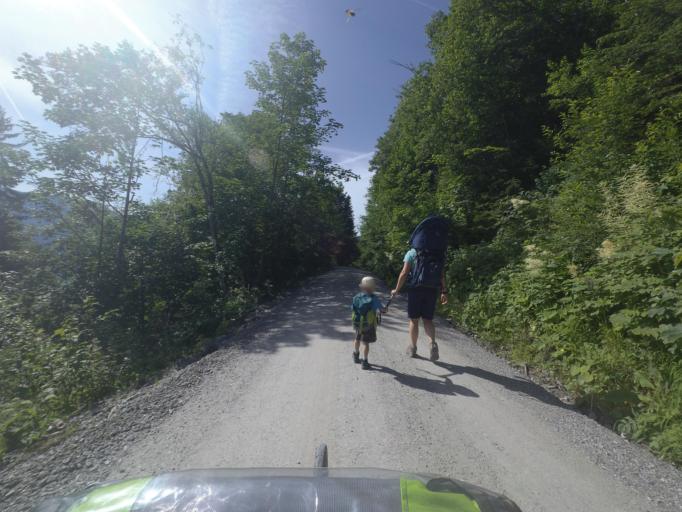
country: AT
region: Salzburg
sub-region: Politischer Bezirk Sankt Johann im Pongau
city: Dorfgastein
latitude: 47.2636
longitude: 13.0747
